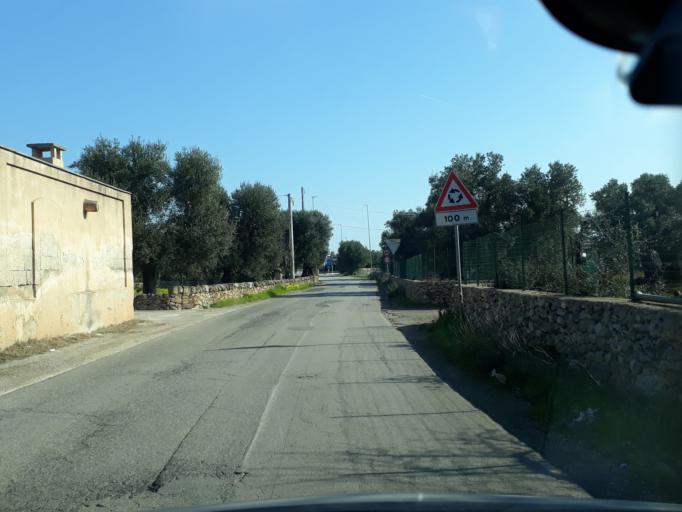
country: IT
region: Apulia
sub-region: Provincia di Brindisi
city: Fasano
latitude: 40.8252
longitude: 17.3826
